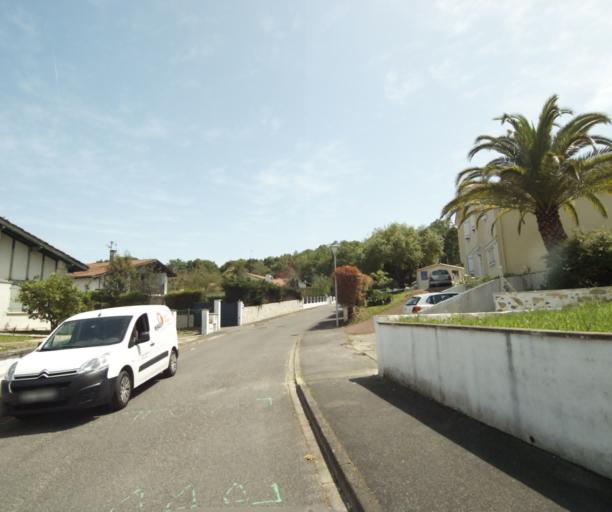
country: FR
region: Aquitaine
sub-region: Departement des Pyrenees-Atlantiques
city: Mouguerre
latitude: 43.4616
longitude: -1.4327
